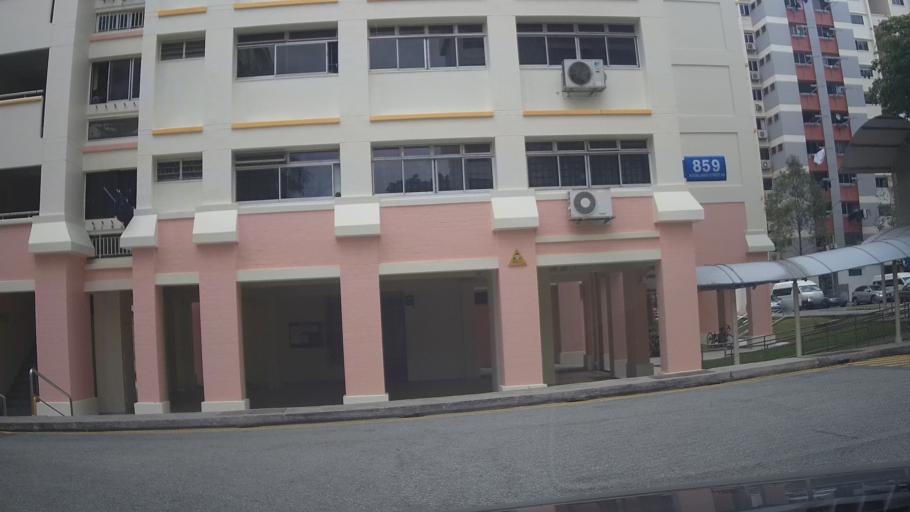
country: MY
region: Johor
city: Johor Bahru
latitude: 1.4402
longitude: 103.7934
